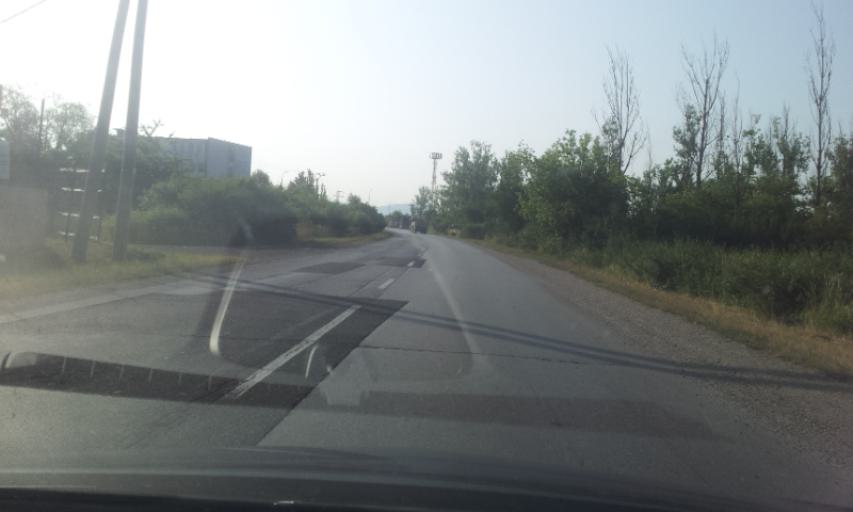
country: SK
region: Kosicky
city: Kosice
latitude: 48.6190
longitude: 21.2316
